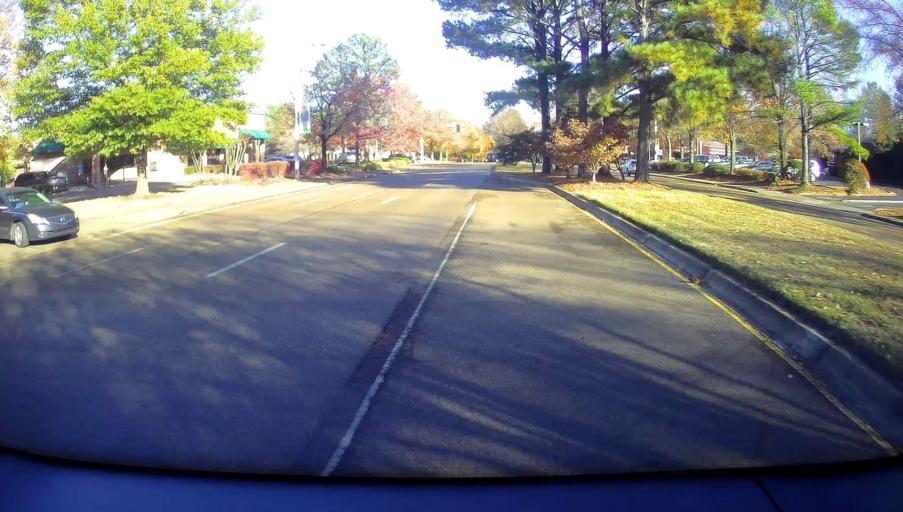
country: US
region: Tennessee
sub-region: Shelby County
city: Germantown
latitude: 35.0958
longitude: -89.8033
